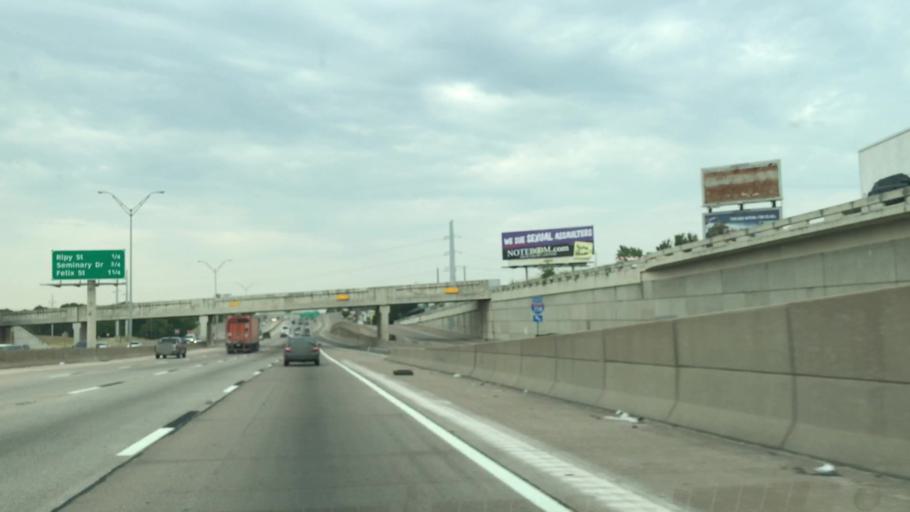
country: US
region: Texas
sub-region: Tarrant County
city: Fort Worth
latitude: 32.7048
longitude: -97.3208
